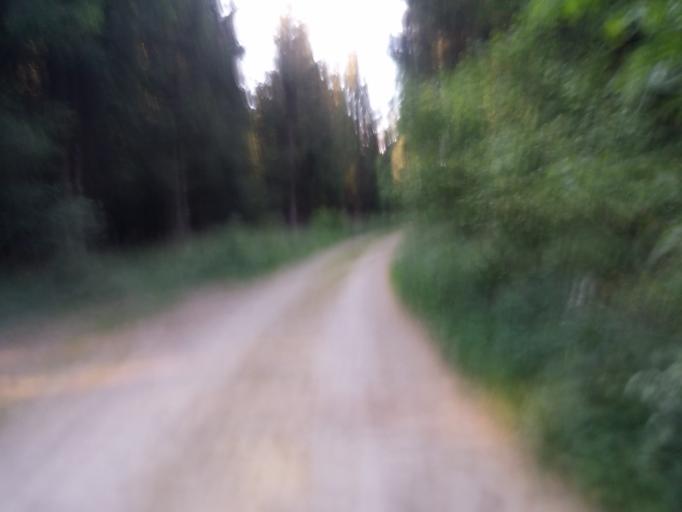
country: DE
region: Bavaria
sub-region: Upper Bavaria
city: Zorneding
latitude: 48.1130
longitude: 11.8164
